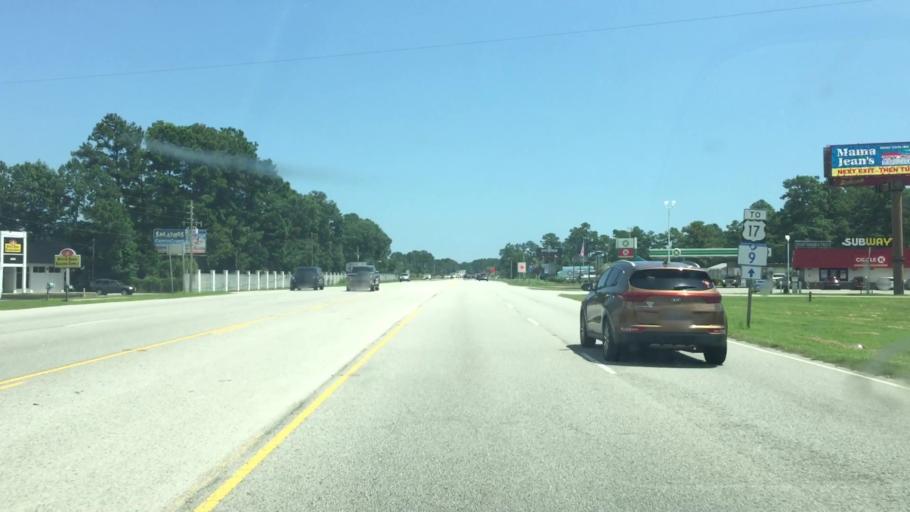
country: US
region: South Carolina
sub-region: Horry County
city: North Myrtle Beach
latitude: 33.8715
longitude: -78.6724
